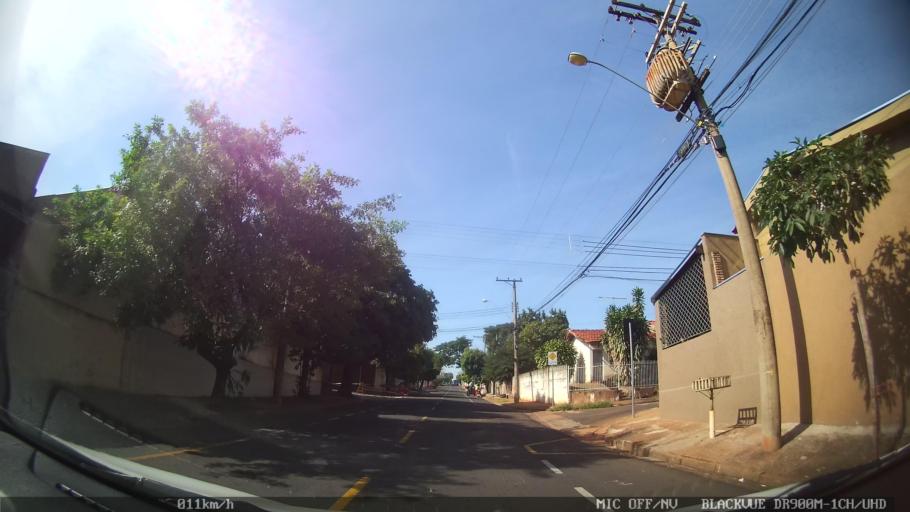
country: BR
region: Sao Paulo
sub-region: Sao Jose Do Rio Preto
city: Sao Jose do Rio Preto
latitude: -20.7955
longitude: -49.4235
